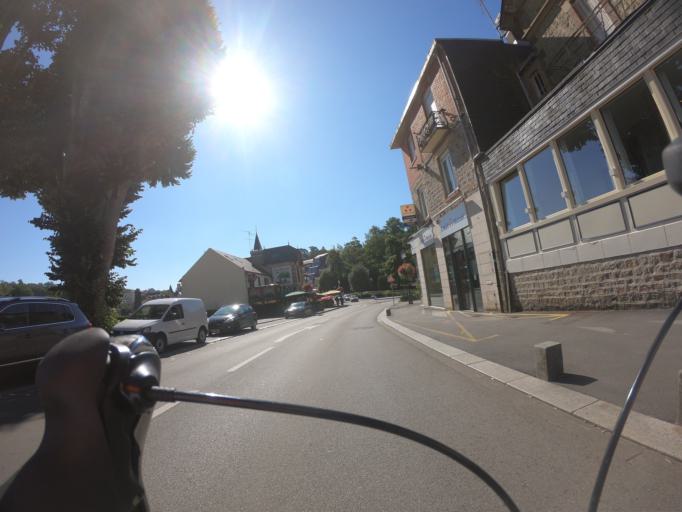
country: FR
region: Lower Normandy
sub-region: Departement de l'Orne
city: Tesse-la-Madeleine
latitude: 48.5574
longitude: -0.4181
